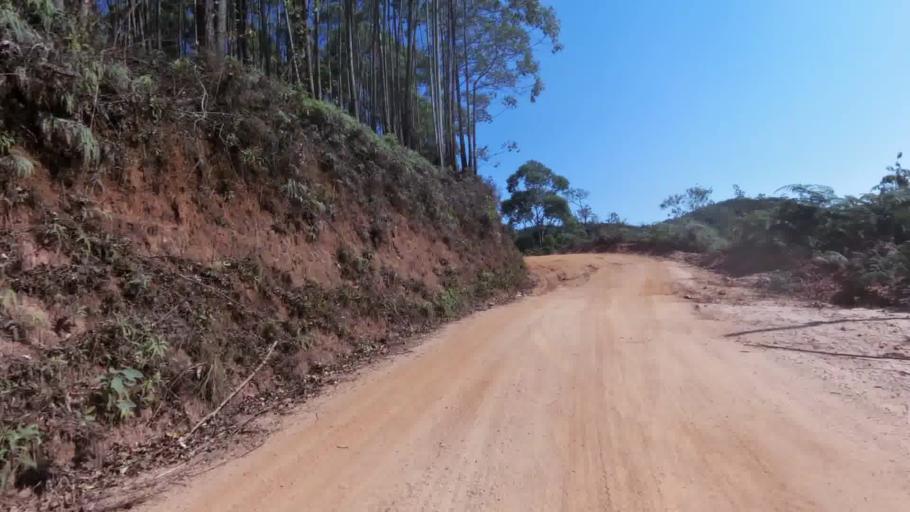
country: BR
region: Espirito Santo
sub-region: Alfredo Chaves
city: Alfredo Chaves
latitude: -20.5180
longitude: -40.8746
